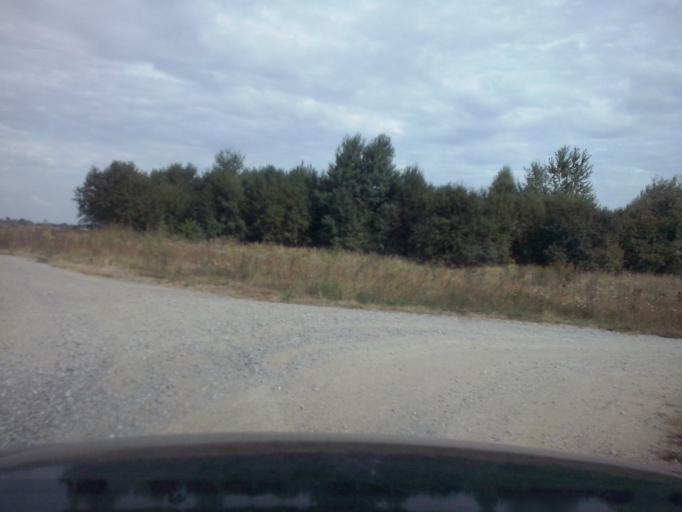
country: PL
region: Swietokrzyskie
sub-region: Powiat kielecki
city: Lagow
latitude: 50.7855
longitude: 21.0878
